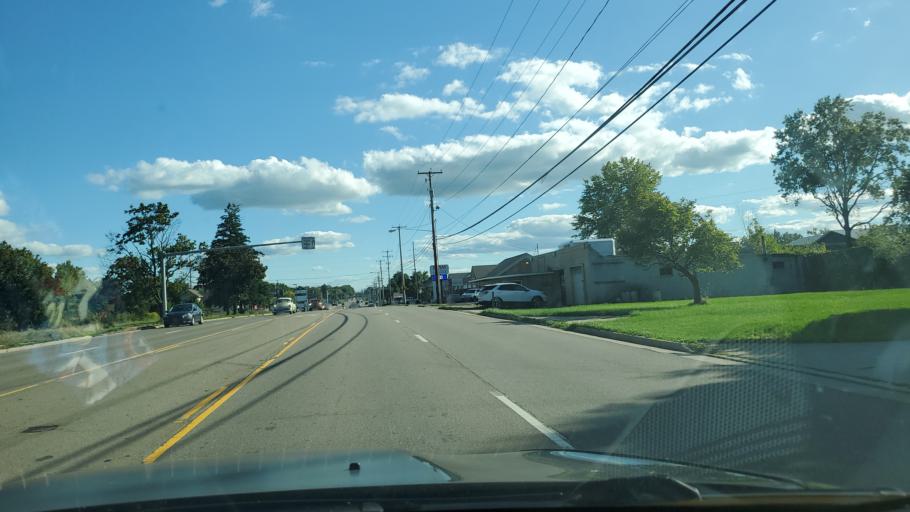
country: US
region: Ohio
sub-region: Mahoning County
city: Austintown
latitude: 41.1039
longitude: -80.7643
